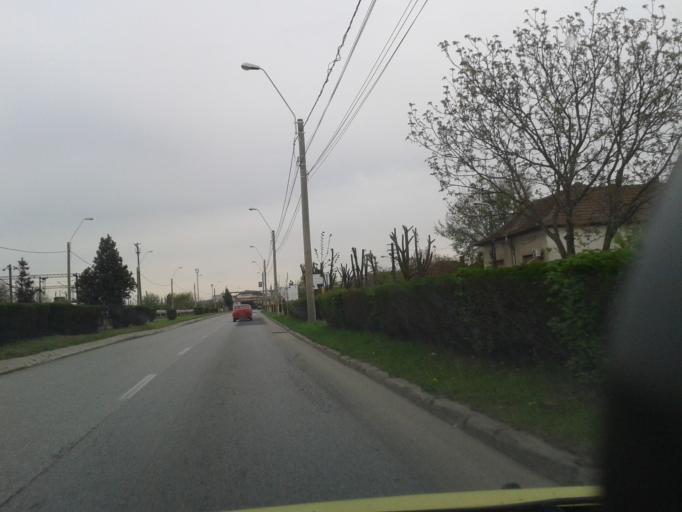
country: RO
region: Hunedoara
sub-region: Municipiul Deva
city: Deva
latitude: 45.8912
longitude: 22.9051
